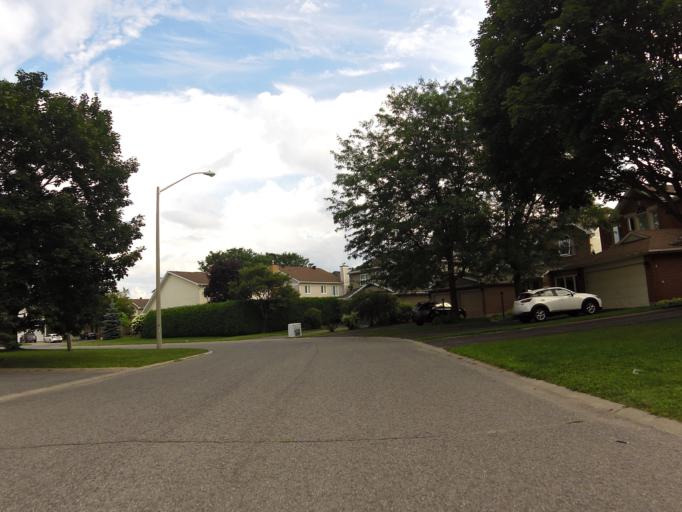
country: CA
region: Ontario
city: Bells Corners
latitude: 45.3422
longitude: -75.7719
